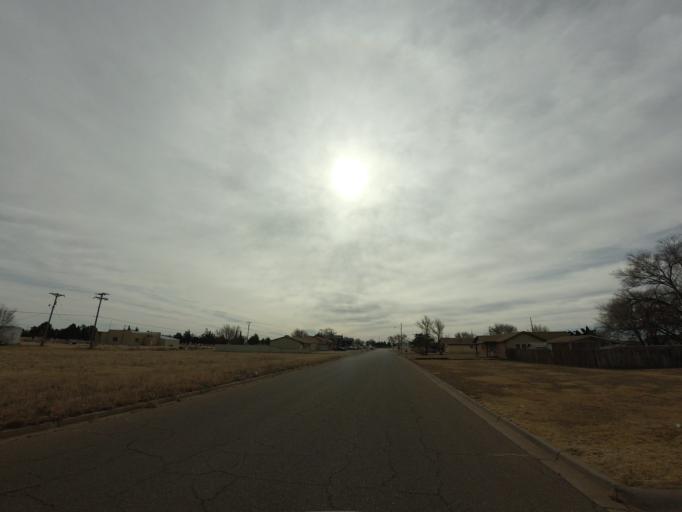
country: US
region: New Mexico
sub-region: Curry County
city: Clovis
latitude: 34.4075
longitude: -103.2457
